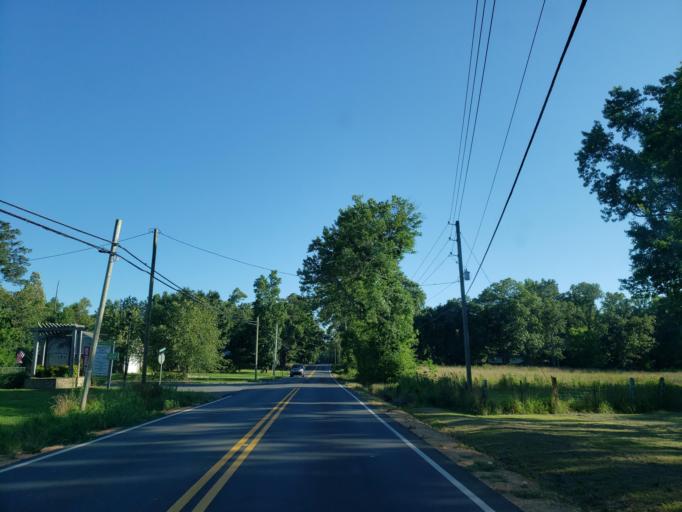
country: US
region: Georgia
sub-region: Floyd County
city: Rome
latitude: 34.3299
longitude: -85.1607
